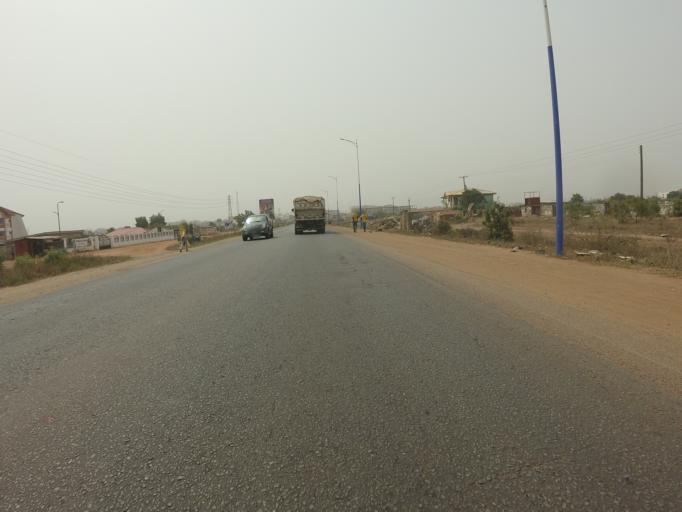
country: GH
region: Greater Accra
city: Tema
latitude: 5.7468
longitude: 0.0401
